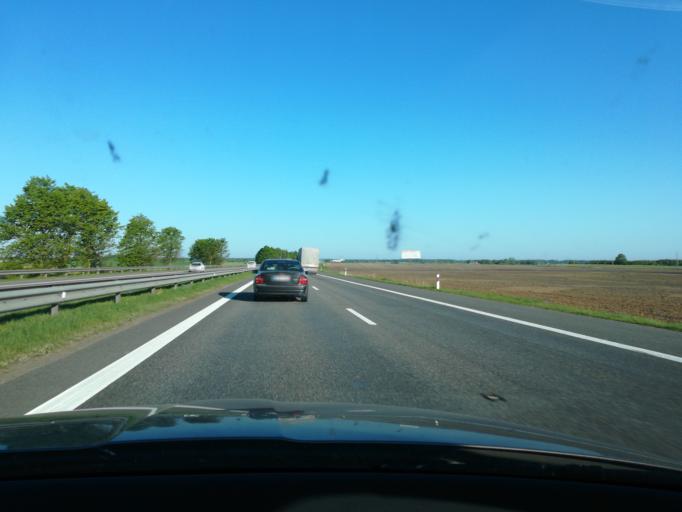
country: LT
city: Kaisiadorys
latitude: 54.8595
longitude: 24.2744
